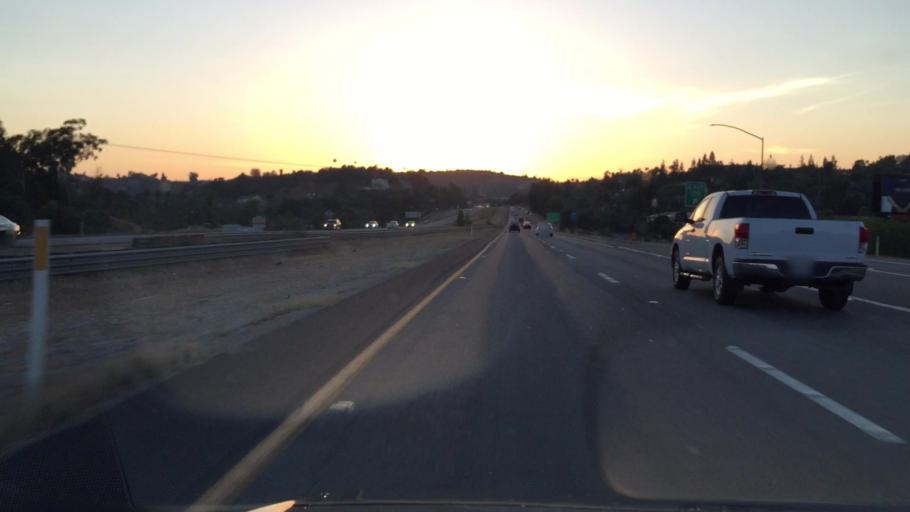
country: US
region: California
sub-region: San Diego County
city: Spring Valley
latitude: 32.7455
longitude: -116.9869
